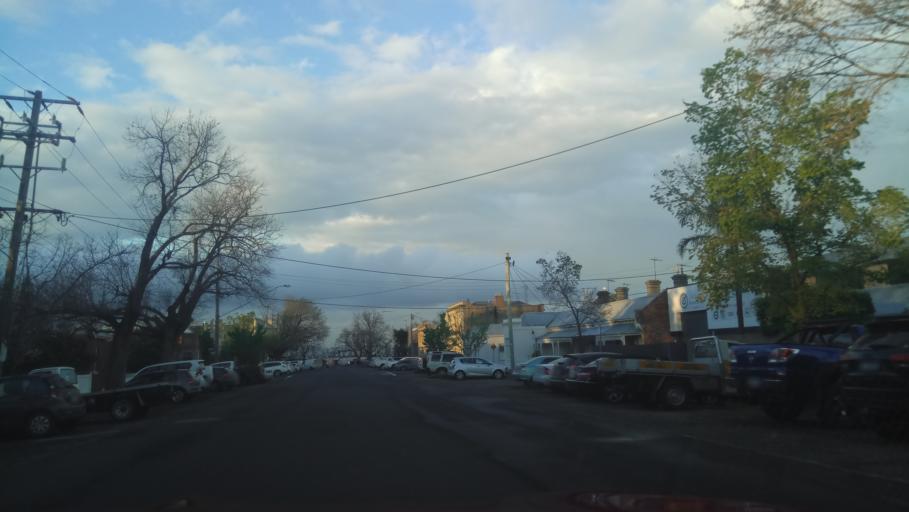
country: AU
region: Victoria
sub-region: Hobsons Bay
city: Williamstown
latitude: -37.8650
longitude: 144.9046
